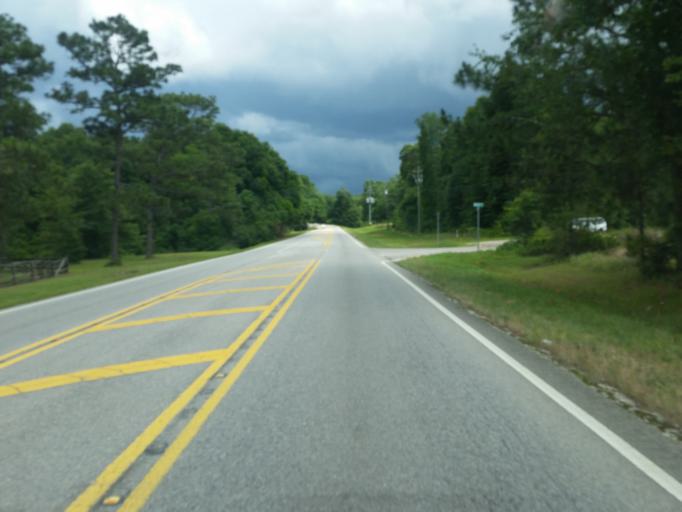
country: US
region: Mississippi
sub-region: Jackson County
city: Hurley
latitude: 30.8302
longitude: -88.3844
